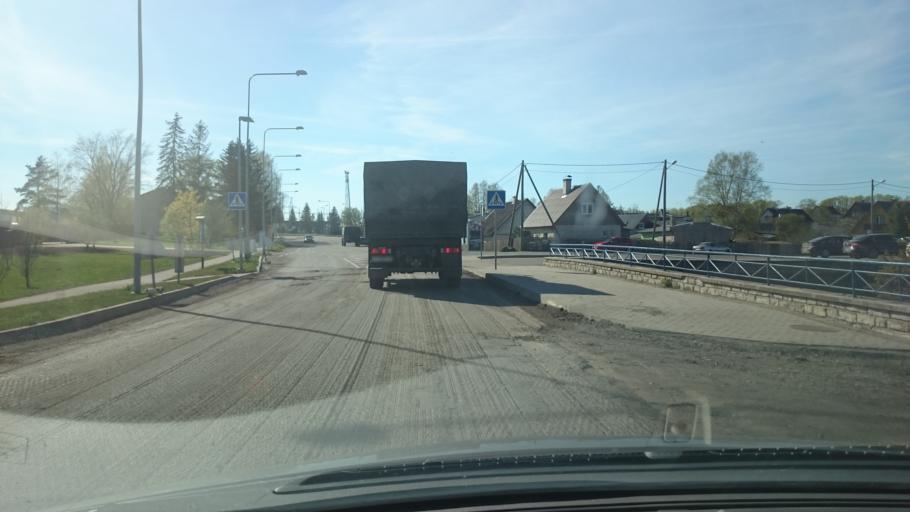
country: EE
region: Laeaene-Virumaa
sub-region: Rakvere linn
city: Rakvere
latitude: 59.3511
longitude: 26.3430
